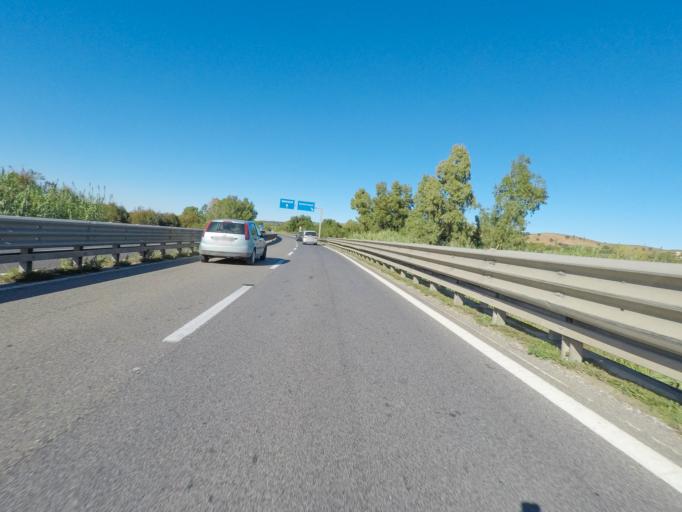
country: IT
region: Tuscany
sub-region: Provincia di Grosseto
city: Grosseto
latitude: 42.7123
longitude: 11.1446
